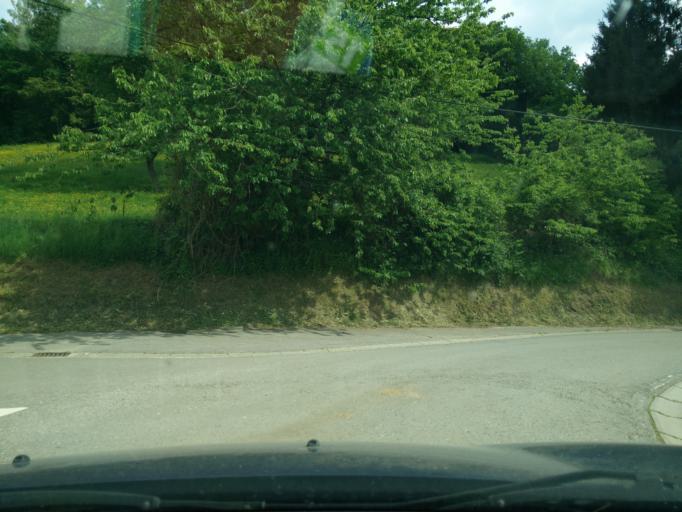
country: FR
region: Champagne-Ardenne
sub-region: Departement des Ardennes
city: Vireux-Molhain
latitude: 50.0834
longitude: 4.6337
